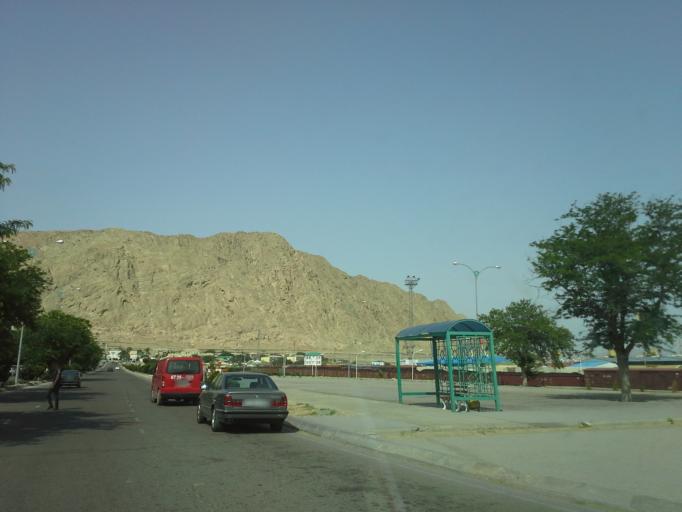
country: TM
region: Balkan
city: Turkmenbasy
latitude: 40.0046
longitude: 52.9954
